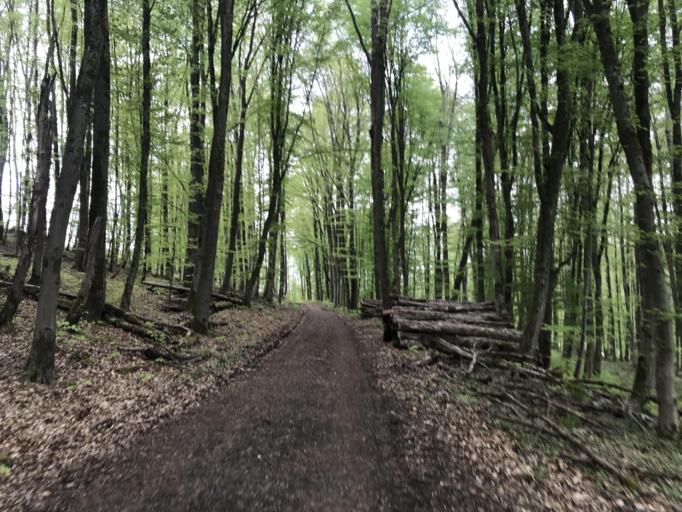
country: DE
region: Hesse
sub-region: Regierungsbezirk Giessen
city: Laubach
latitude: 50.5175
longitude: 8.9912
